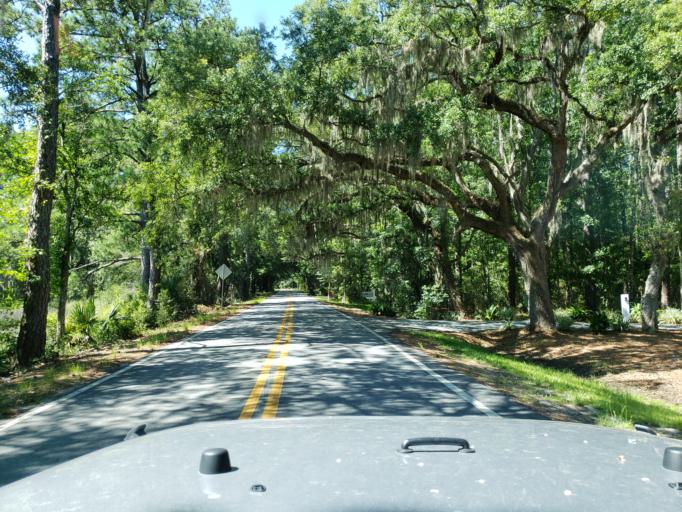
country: US
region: Georgia
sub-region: Chatham County
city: Georgetown
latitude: 31.9668
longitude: -81.2185
